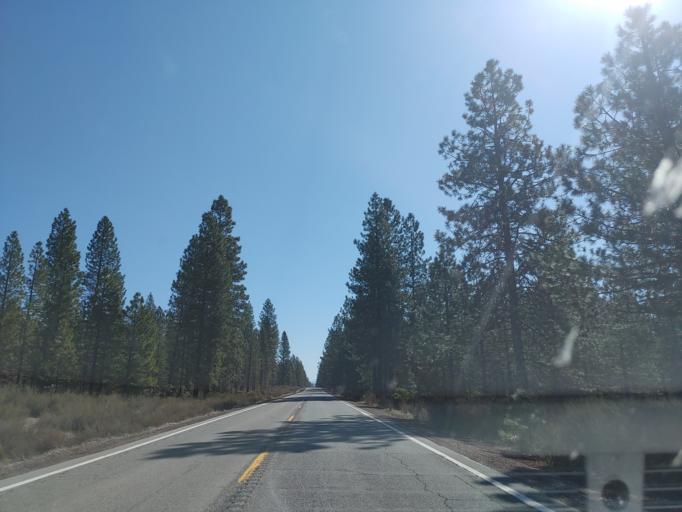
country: US
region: California
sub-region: Siskiyou County
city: McCloud
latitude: 41.2519
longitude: -122.1136
